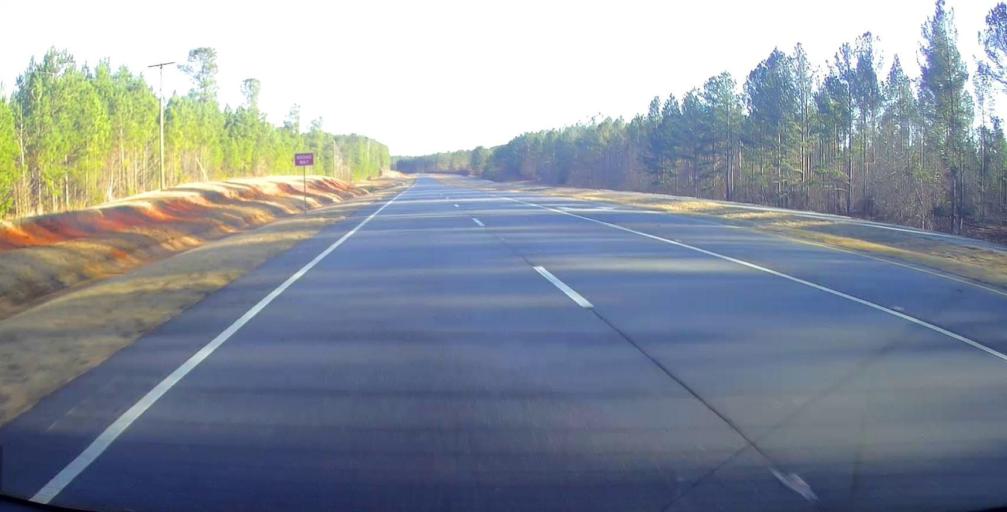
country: US
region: Georgia
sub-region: Upson County
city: Thomaston
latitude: 32.8037
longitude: -84.2761
